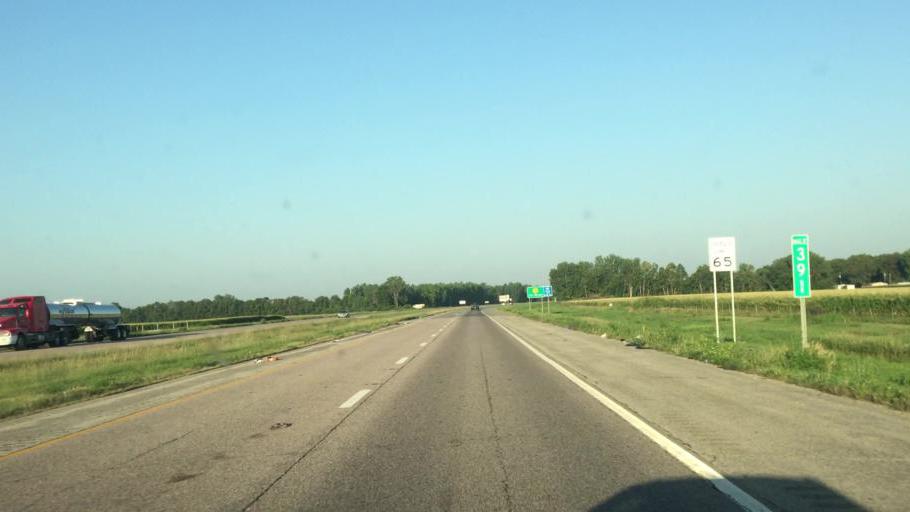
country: US
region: Kansas
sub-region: Doniphan County
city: Elwood
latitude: 39.7469
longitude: -94.8766
